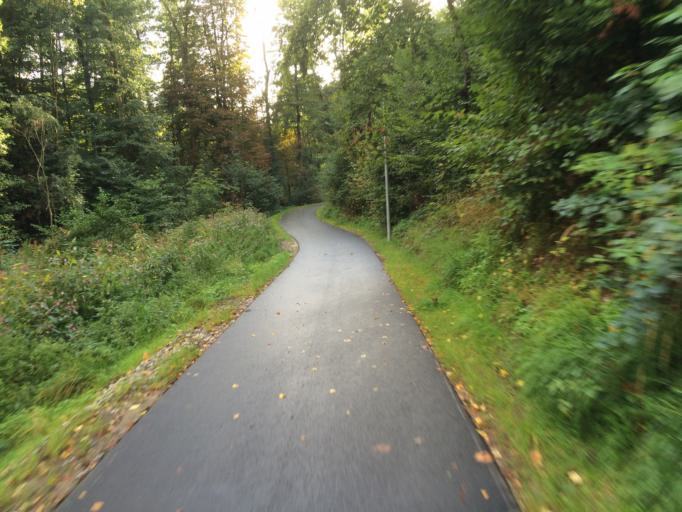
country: DE
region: North Rhine-Westphalia
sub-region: Regierungsbezirk Detmold
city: Detmold
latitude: 51.9243
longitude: 8.8655
